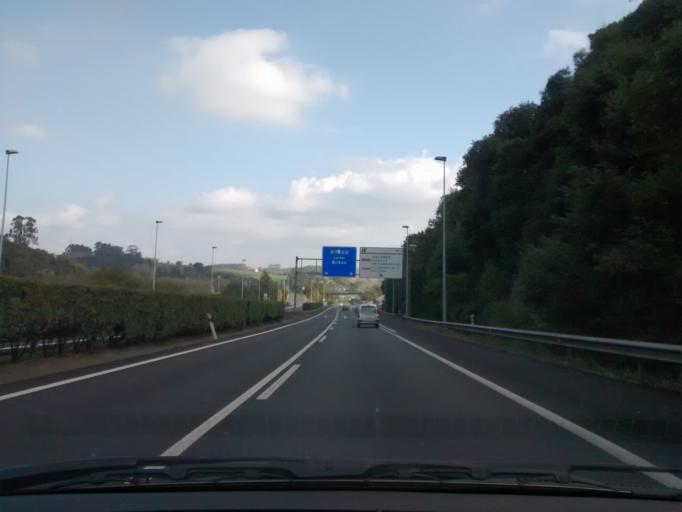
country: ES
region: Cantabria
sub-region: Provincia de Cantabria
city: Entrambasaguas
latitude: 43.3905
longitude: -3.7126
